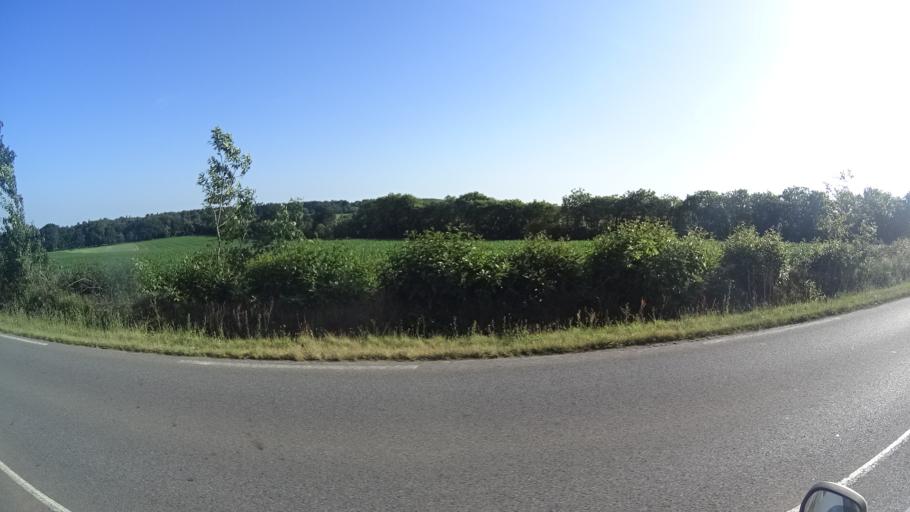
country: FR
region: Brittany
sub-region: Departement du Morbihan
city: Saint-Jean-la-Poterie
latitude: 47.6118
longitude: -2.1432
